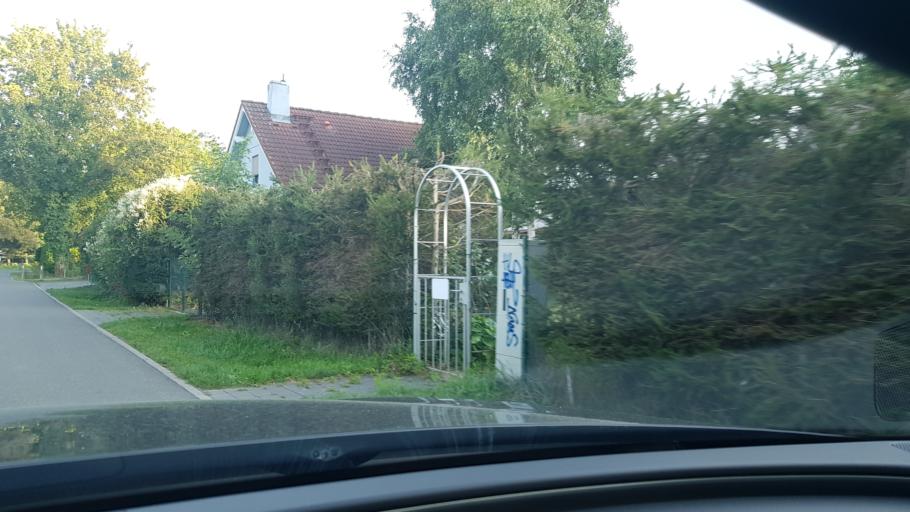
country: DE
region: Brandenburg
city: Brieselang
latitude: 52.5896
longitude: 12.9885
